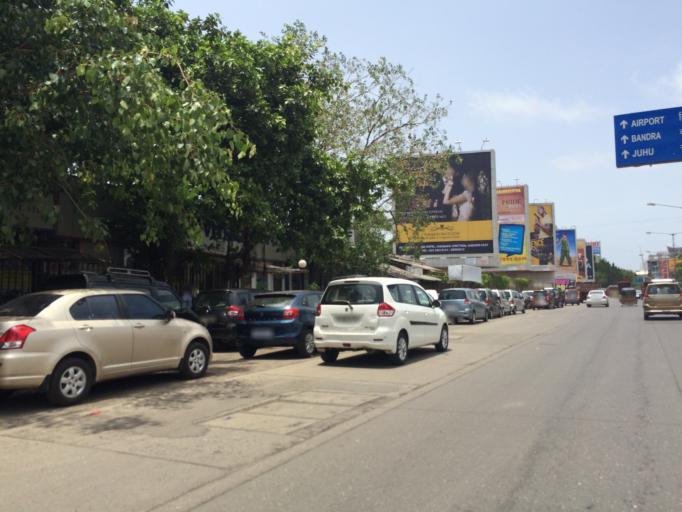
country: IN
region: Maharashtra
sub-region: Mumbai Suburban
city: Powai
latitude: 19.1345
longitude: 72.8320
